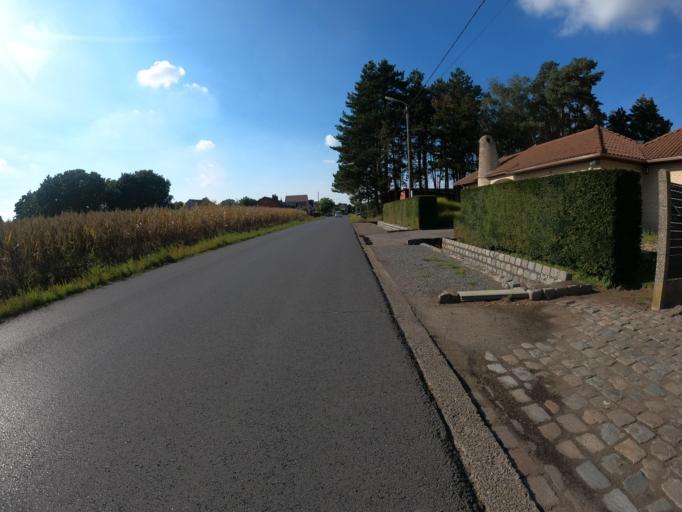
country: BE
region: Flanders
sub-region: Provincie Antwerpen
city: Berlaar
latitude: 51.0801
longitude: 4.6607
